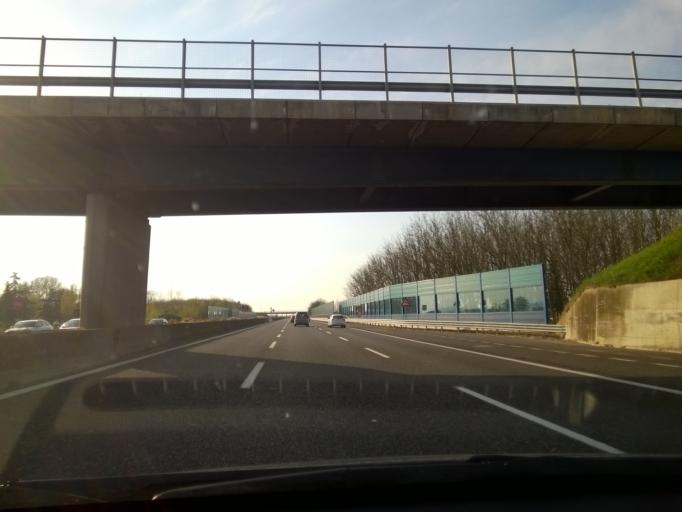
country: IT
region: Emilia-Romagna
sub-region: Provincia di Ravenna
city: Granarolo
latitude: 44.3002
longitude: 11.9628
